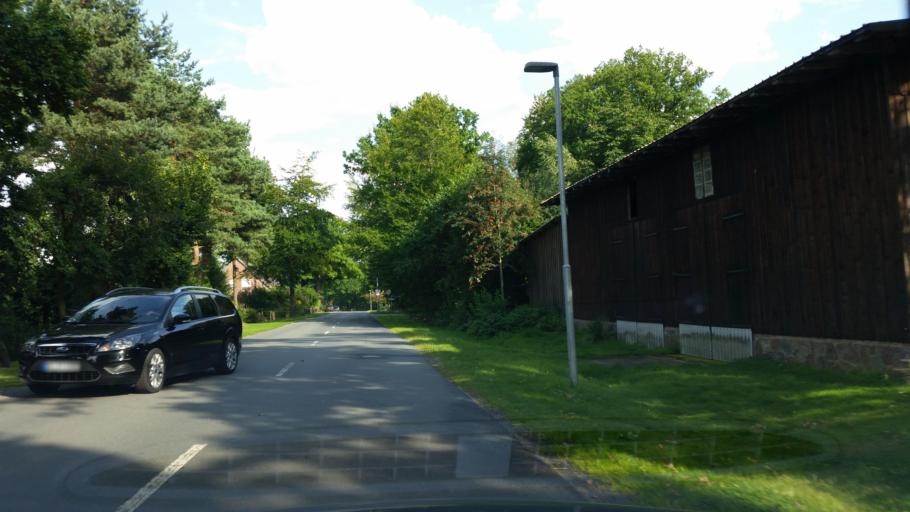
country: DE
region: Lower Saxony
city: Neuenkirchen
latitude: 53.0569
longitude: 9.7414
